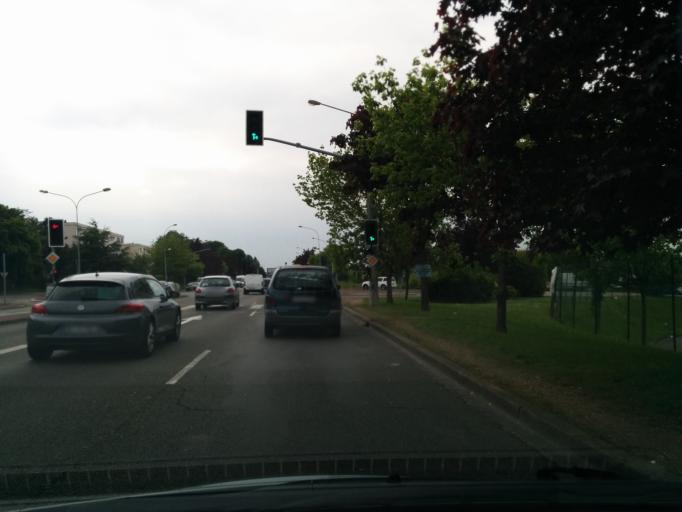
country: FR
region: Ile-de-France
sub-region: Departement des Yvelines
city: Aubergenville
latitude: 48.9636
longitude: 1.8633
